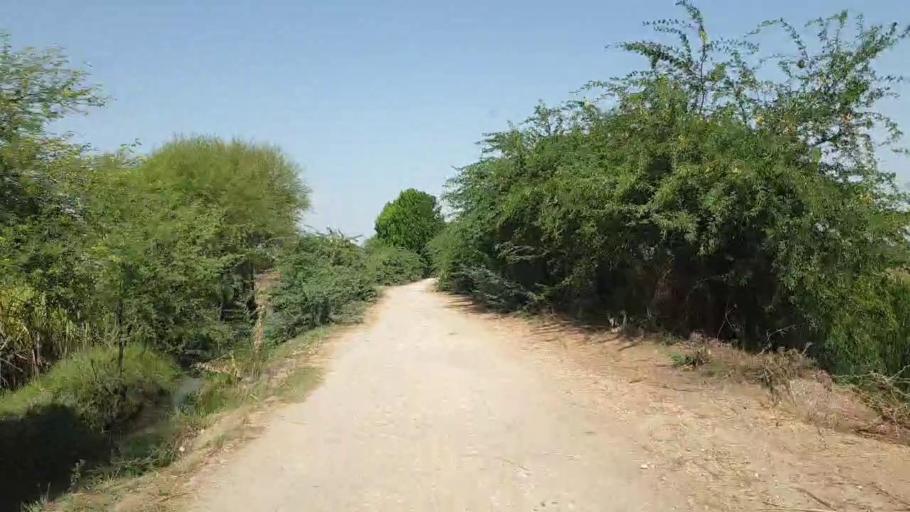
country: PK
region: Sindh
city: Tando Bago
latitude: 24.7608
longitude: 69.0239
